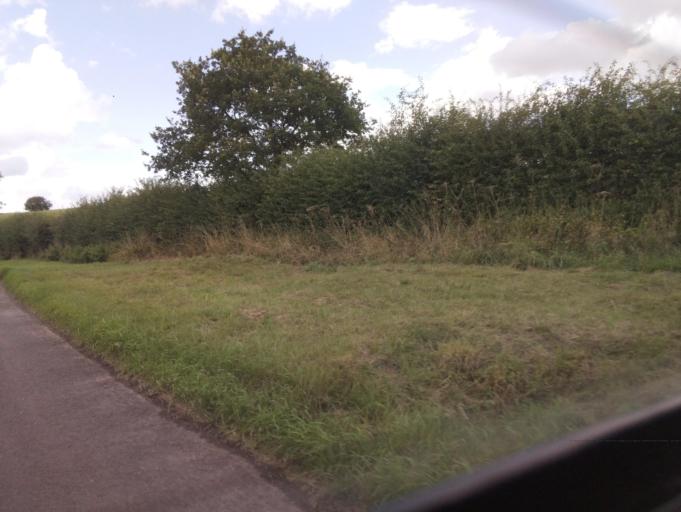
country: GB
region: England
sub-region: North Yorkshire
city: Bedale
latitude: 54.2514
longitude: -1.6979
